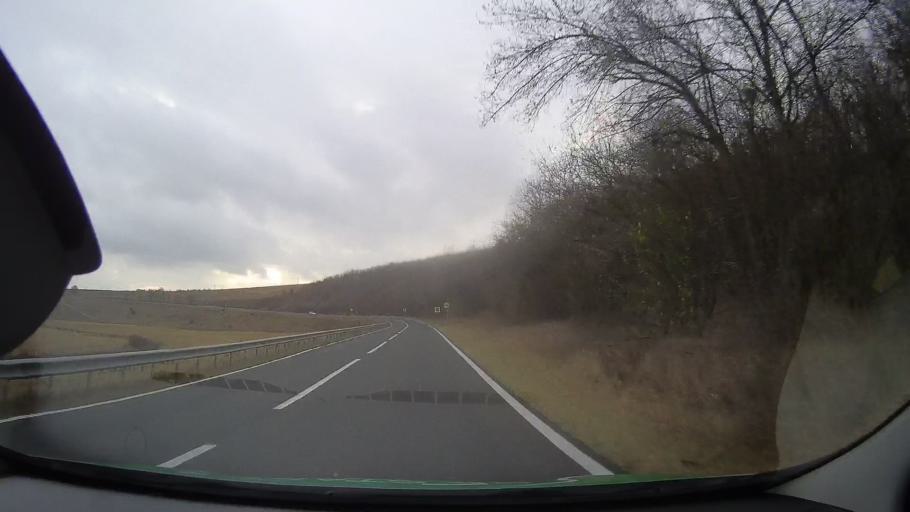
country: RO
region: Constanta
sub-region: Comuna Deleni
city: Deleni
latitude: 44.0994
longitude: 28.0205
